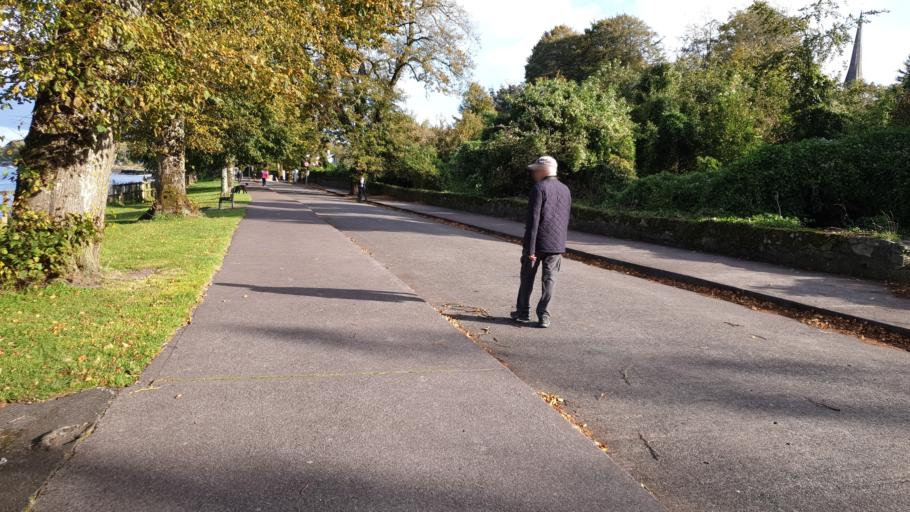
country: IE
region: Munster
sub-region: County Cork
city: Cork
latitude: 51.8985
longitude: -8.4186
